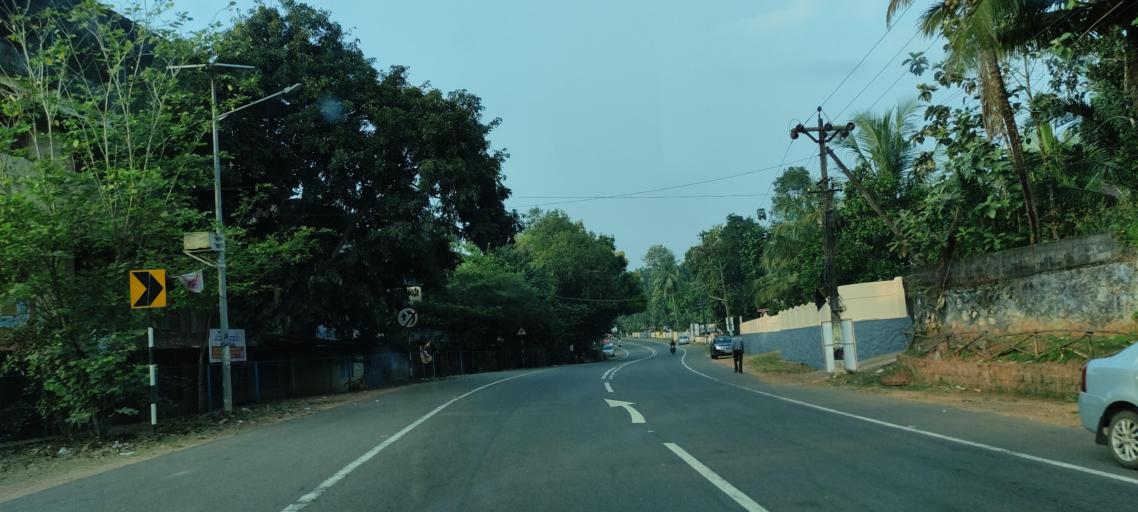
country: IN
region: Kerala
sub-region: Pattanamtitta
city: Adur
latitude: 9.1393
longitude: 76.7343
